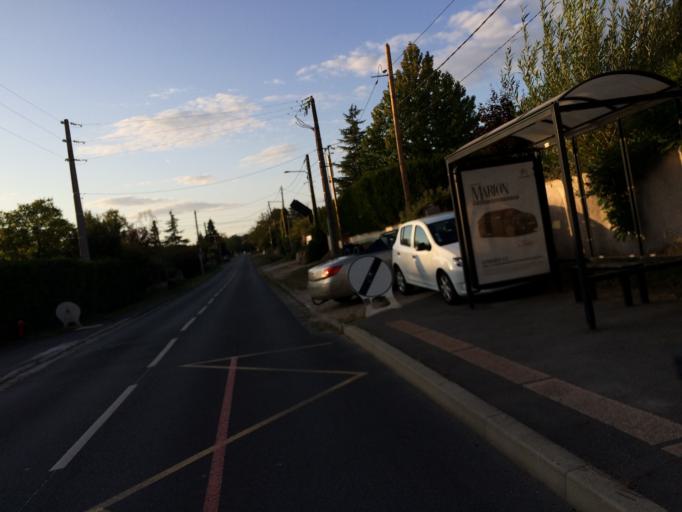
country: FR
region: Ile-de-France
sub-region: Departement de l'Essonne
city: Nozay
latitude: 48.6555
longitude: 2.2103
